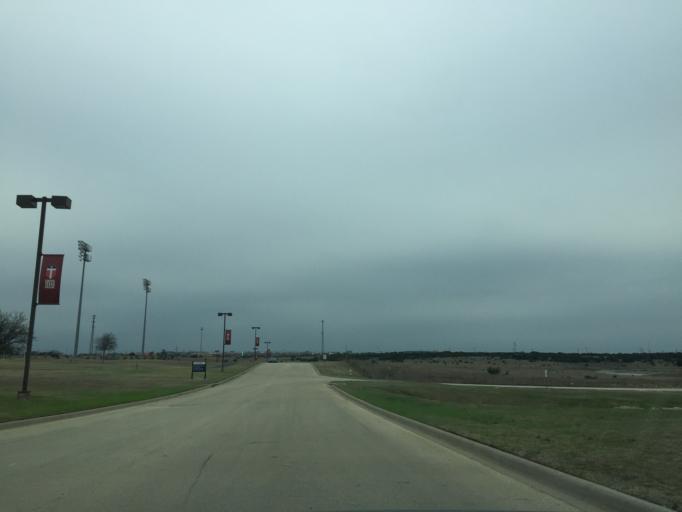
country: US
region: Texas
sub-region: Bell County
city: Fort Hood
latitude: 31.1156
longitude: -97.8079
